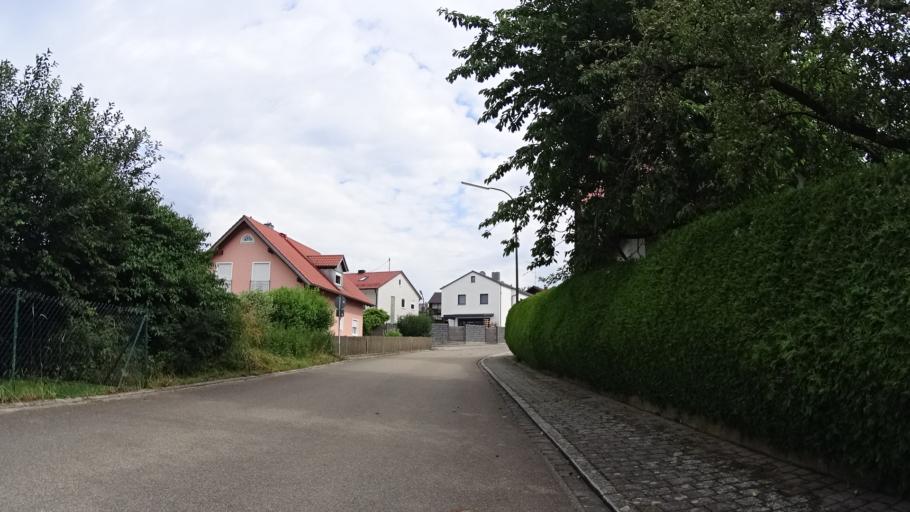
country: DE
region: Bavaria
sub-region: Upper Bavaria
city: Stammham
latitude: 48.8527
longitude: 11.4494
